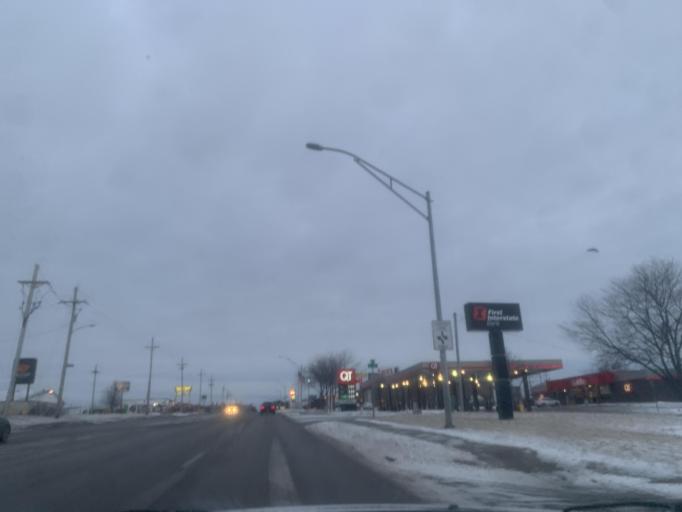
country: US
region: Nebraska
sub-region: Douglas County
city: Ralston
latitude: 41.2187
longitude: -96.0432
